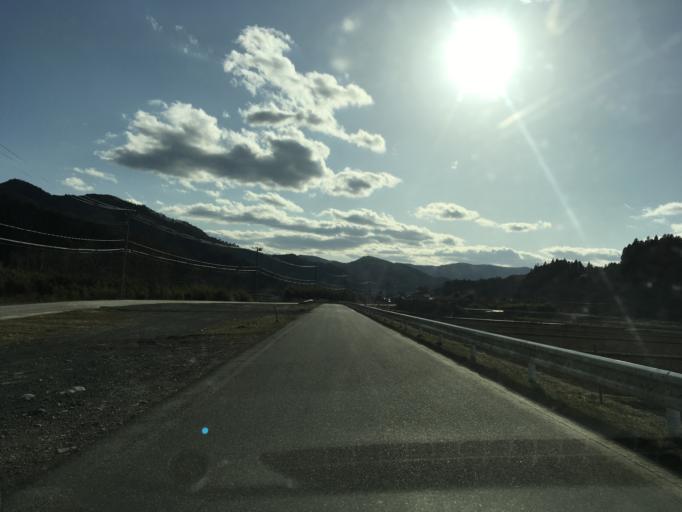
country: JP
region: Iwate
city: Ofunato
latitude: 39.0303
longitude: 141.6005
